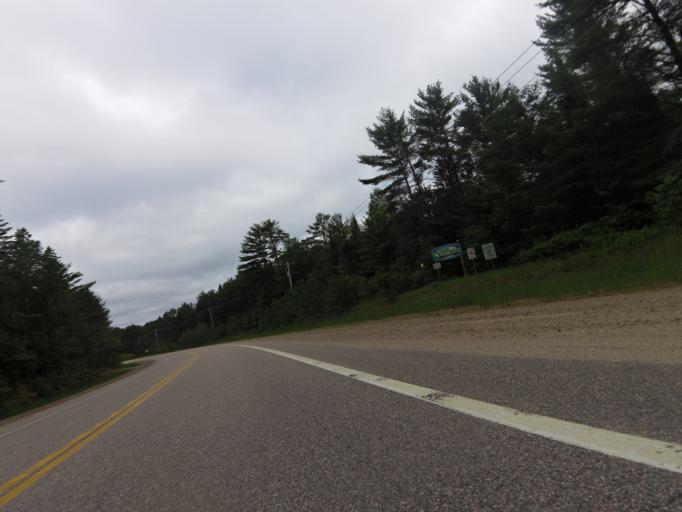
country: CA
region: Quebec
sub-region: Outaouais
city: Shawville
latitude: 45.8593
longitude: -76.4221
